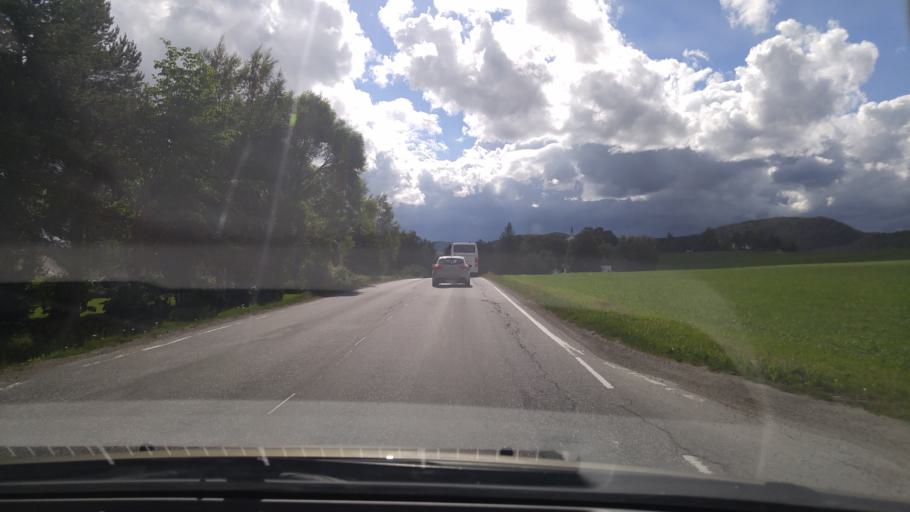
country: NO
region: Nord-Trondelag
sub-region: Namdalseid
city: Namdalseid
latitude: 64.2199
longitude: 11.2222
